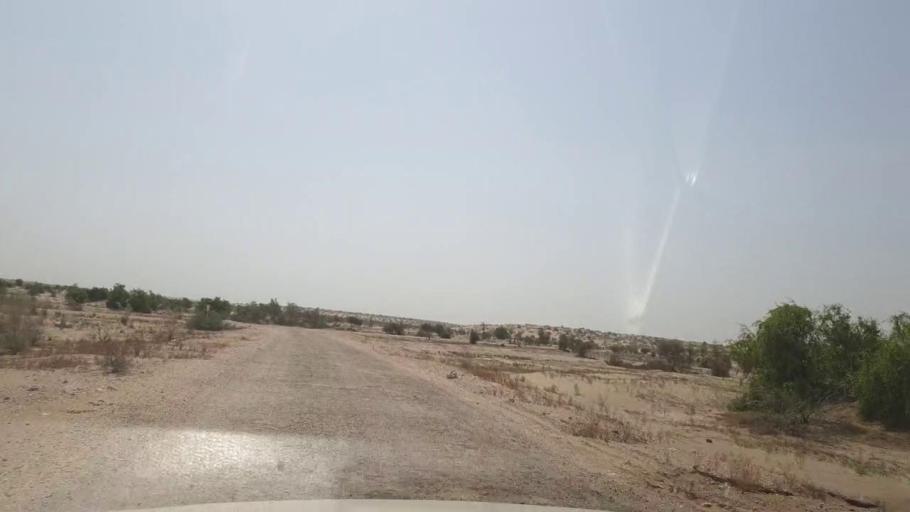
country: PK
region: Sindh
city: Khanpur
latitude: 27.4079
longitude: 69.3233
